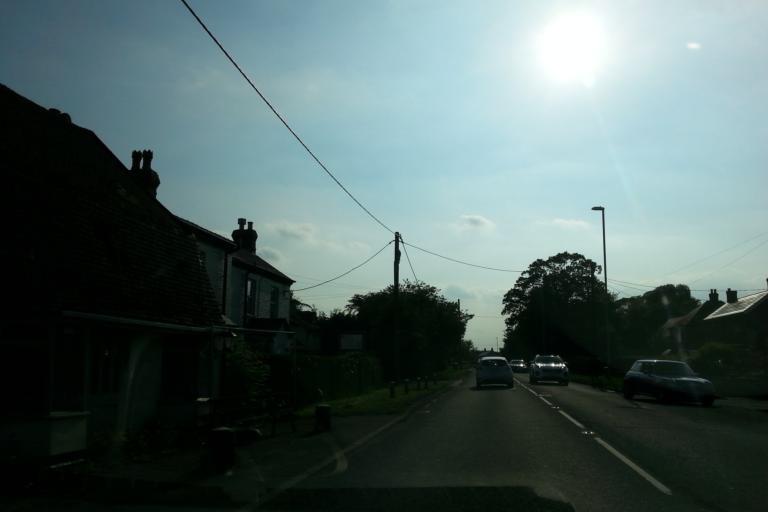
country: GB
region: England
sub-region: Cambridgeshire
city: Earith
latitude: 52.3512
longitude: 0.0103
